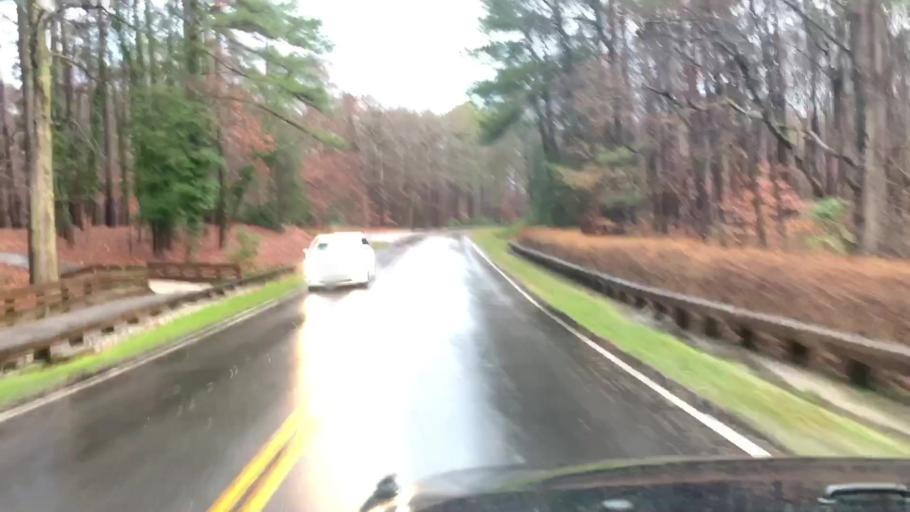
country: US
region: Virginia
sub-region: City of Williamsburg
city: Williamsburg
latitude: 37.2384
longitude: -76.6607
